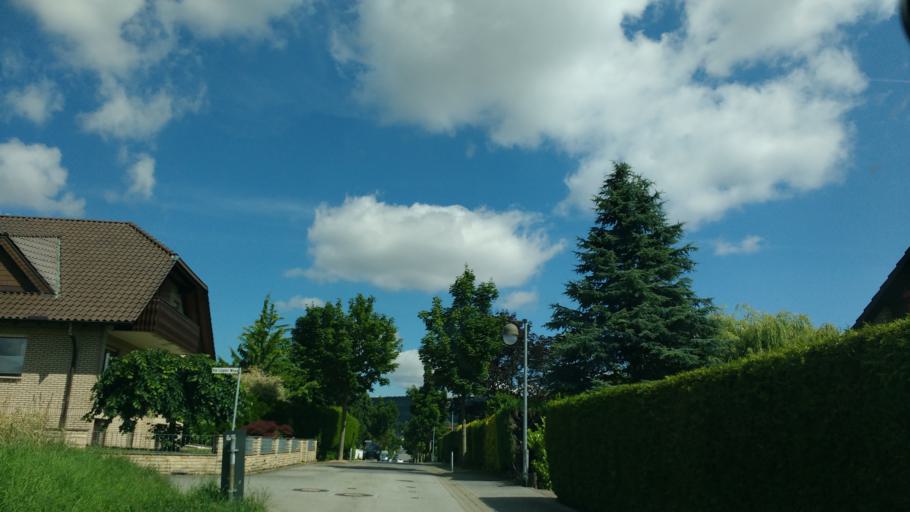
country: DE
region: Lower Saxony
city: Bad Pyrmont
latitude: 51.9791
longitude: 9.2276
